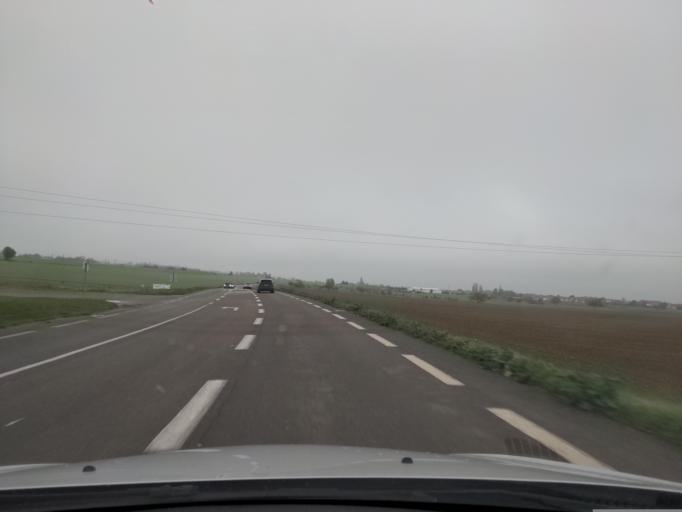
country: FR
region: Bourgogne
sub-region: Departement de la Cote-d'Or
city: Ruffey-les-Echirey
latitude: 47.3591
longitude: 5.0669
